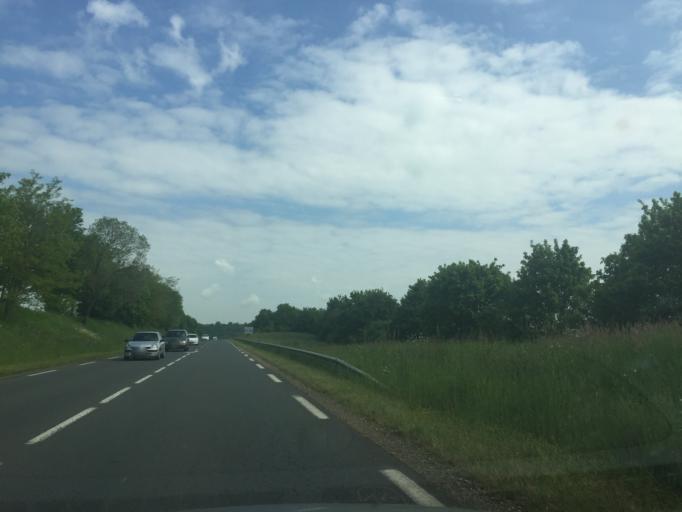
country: FR
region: Poitou-Charentes
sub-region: Departement de la Vienne
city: Lusignan
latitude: 46.4374
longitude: 0.1382
